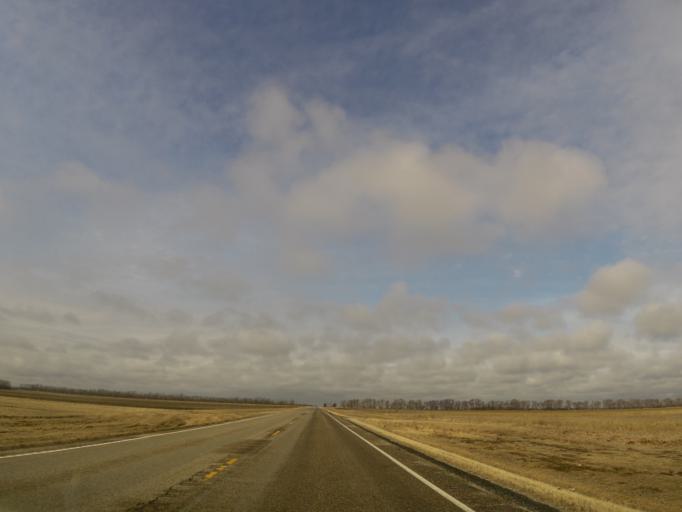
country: US
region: North Dakota
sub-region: Traill County
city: Hillsboro
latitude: 47.4979
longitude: -97.1224
